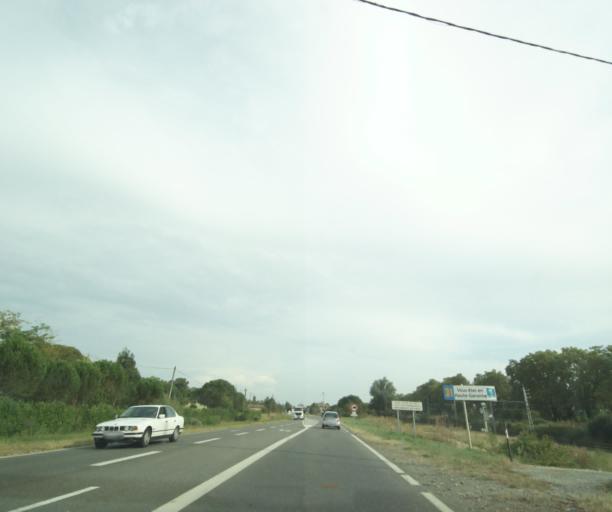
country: FR
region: Midi-Pyrenees
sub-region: Departement du Tarn-et-Garonne
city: Pompignan
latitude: 43.8067
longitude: 1.3221
